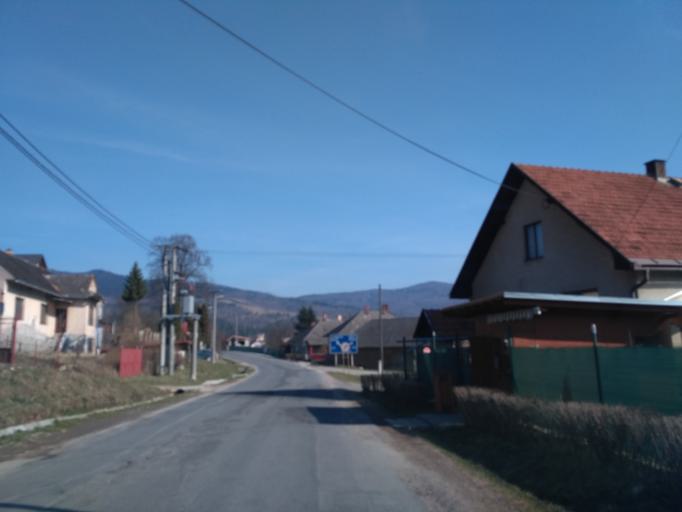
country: SK
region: Kosicky
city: Medzev
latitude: 48.7996
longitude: 20.8071
